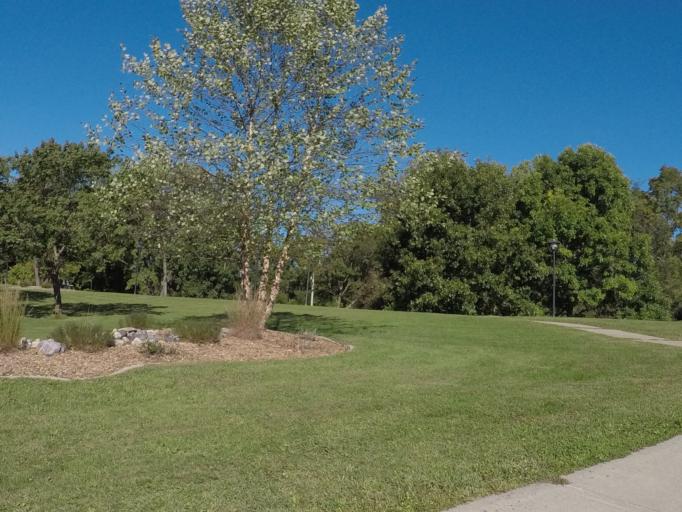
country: US
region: Wisconsin
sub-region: Richland County
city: Richland Center
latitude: 43.3445
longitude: -90.3890
